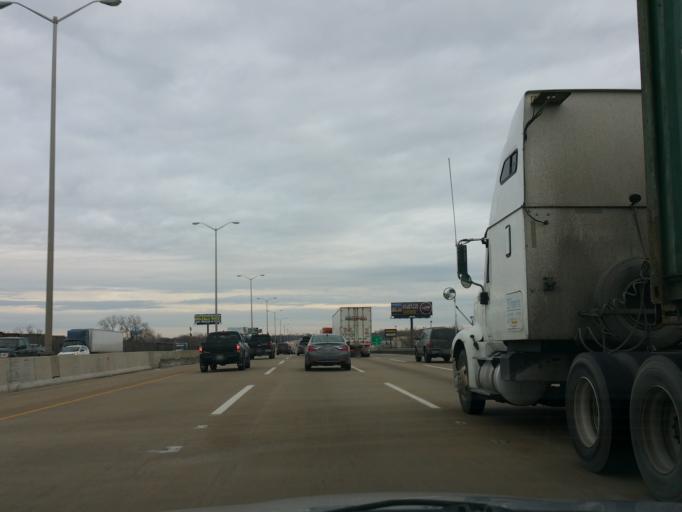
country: US
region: Illinois
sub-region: Cook County
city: Chicago Ridge
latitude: 41.7112
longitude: -87.7981
